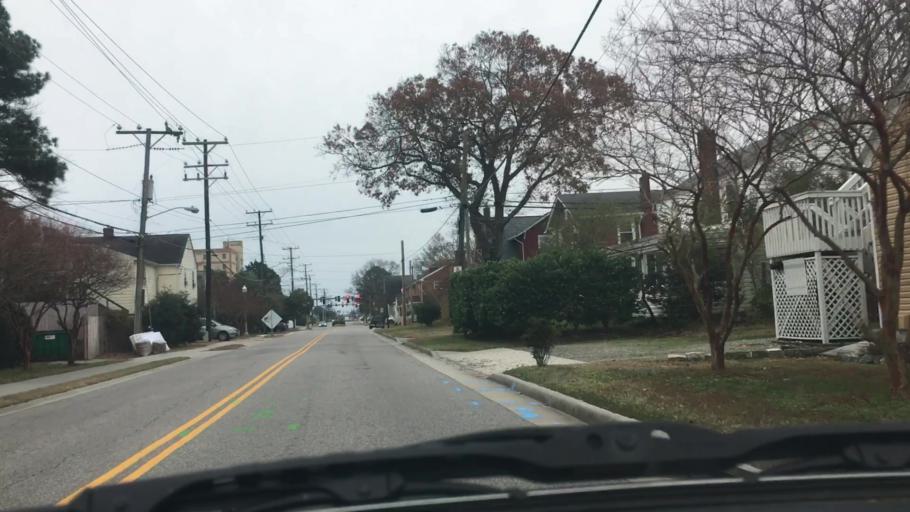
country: US
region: Virginia
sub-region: City of Virginia Beach
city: Virginia Beach
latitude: 36.8515
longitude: -75.9792
